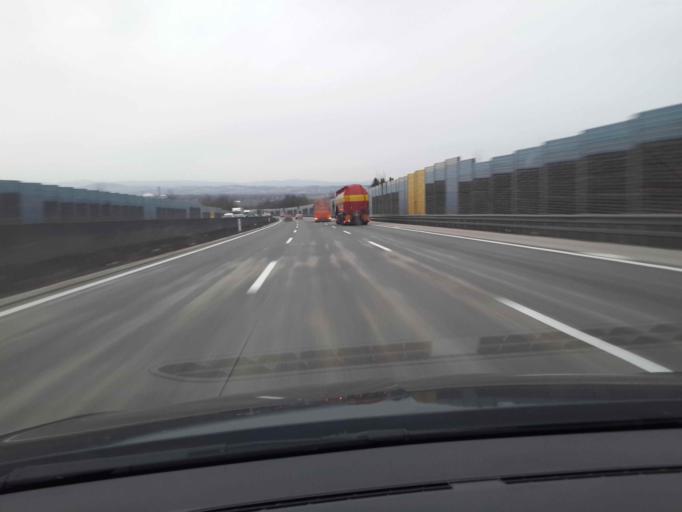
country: AT
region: Lower Austria
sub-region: Politischer Bezirk Amstetten
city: Sankt Valentin
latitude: 48.1750
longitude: 14.5471
